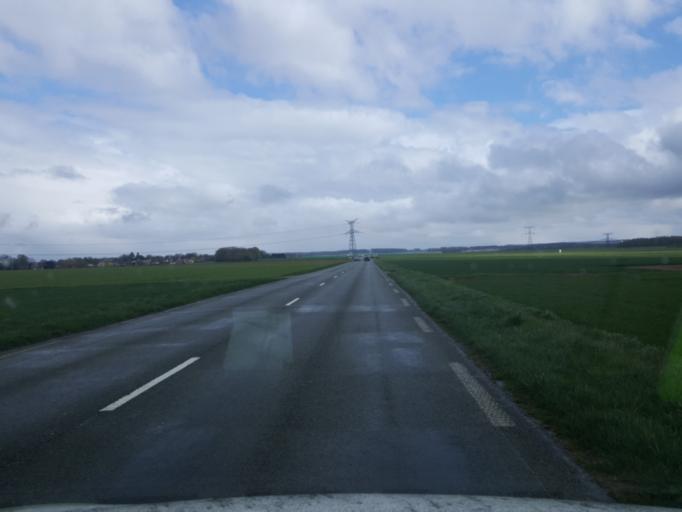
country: FR
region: Picardie
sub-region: Departement de l'Oise
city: Chaumont-en-Vexin
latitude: 49.3129
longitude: 1.8801
